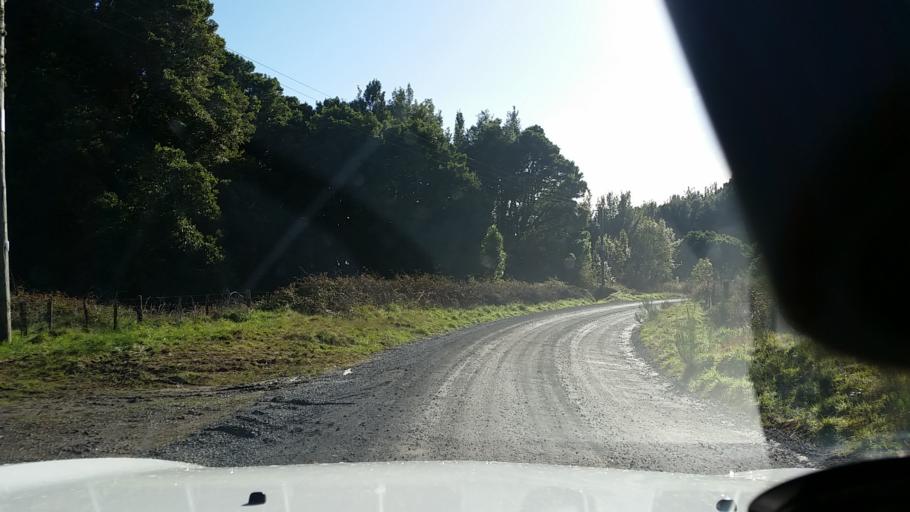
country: NZ
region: Bay of Plenty
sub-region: Kawerau District
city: Kawerau
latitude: -38.0123
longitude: 176.4898
